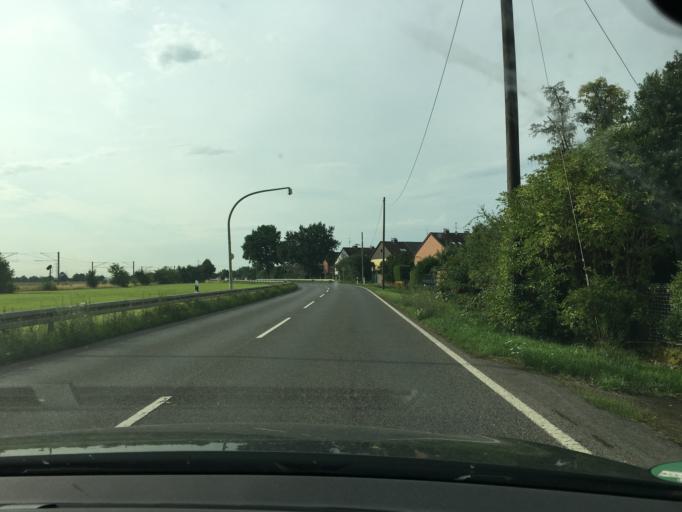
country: DE
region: North Rhine-Westphalia
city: Niederkassel
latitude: 50.7838
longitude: 7.0303
